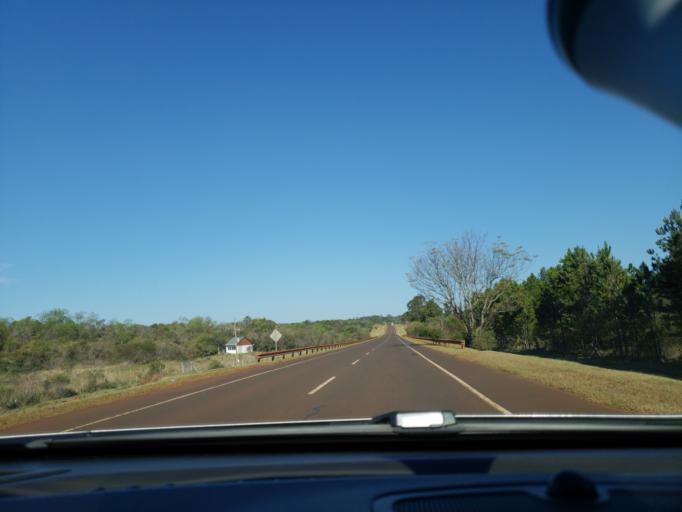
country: AR
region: Misiones
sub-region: Departamento de Apostoles
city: Apostoles
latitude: -27.8442
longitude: -55.7660
